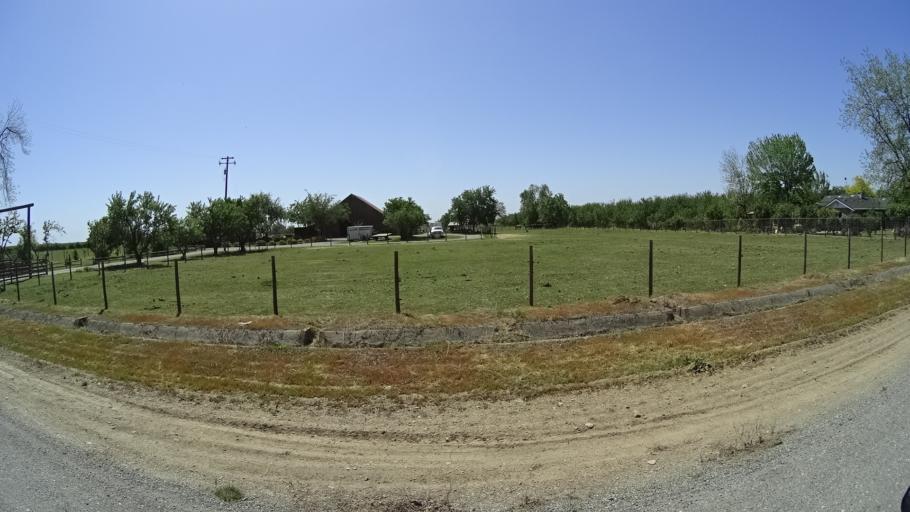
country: US
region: California
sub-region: Glenn County
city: Orland
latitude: 39.7654
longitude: -122.1803
